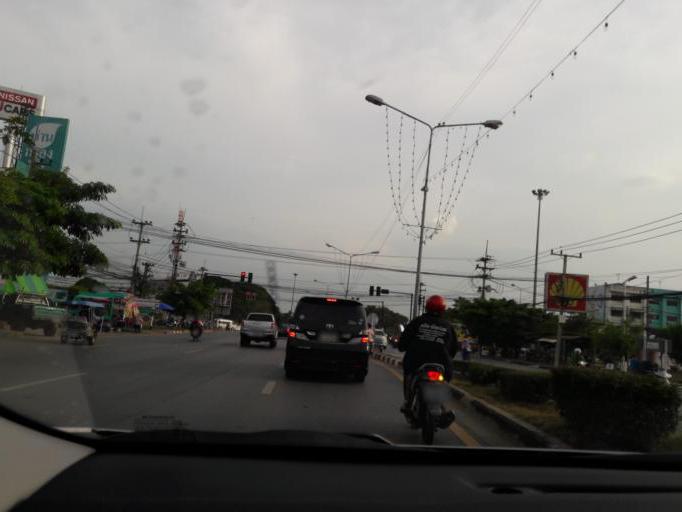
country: TH
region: Ang Thong
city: Ang Thong
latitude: 14.5861
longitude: 100.4553
